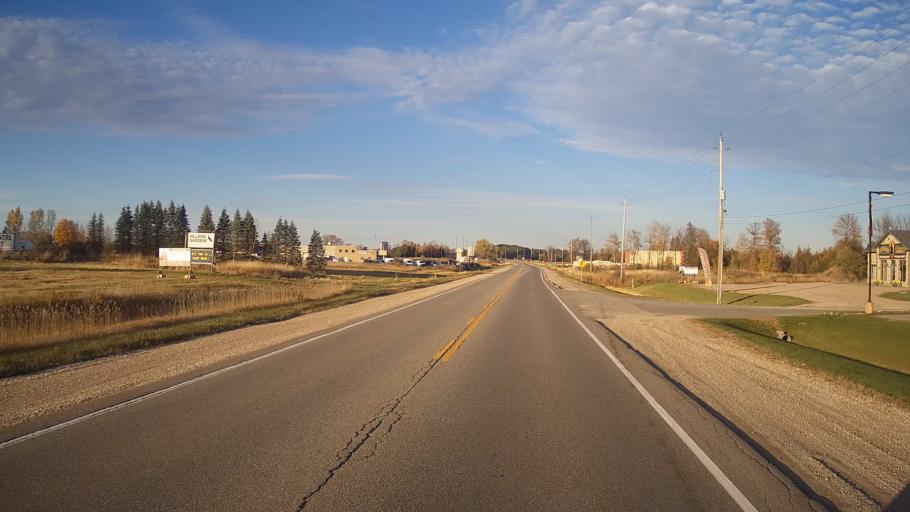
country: CA
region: Ontario
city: Perth
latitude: 44.9296
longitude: -76.2458
